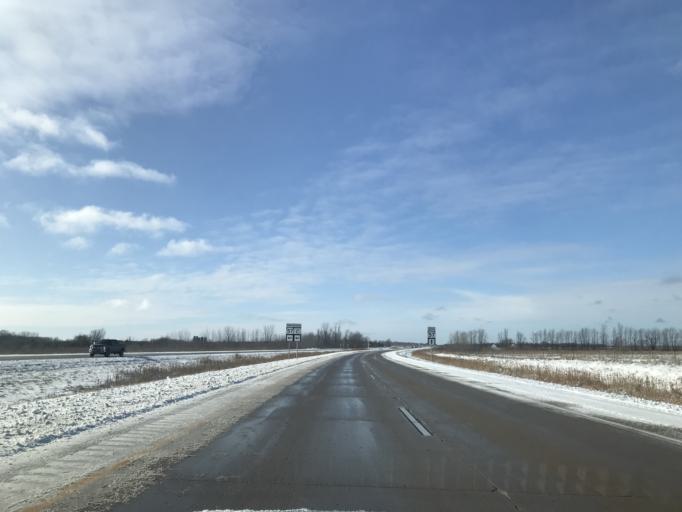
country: US
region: Wisconsin
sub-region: Kewaunee County
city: Luxemburg
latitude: 44.7165
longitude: -87.6254
